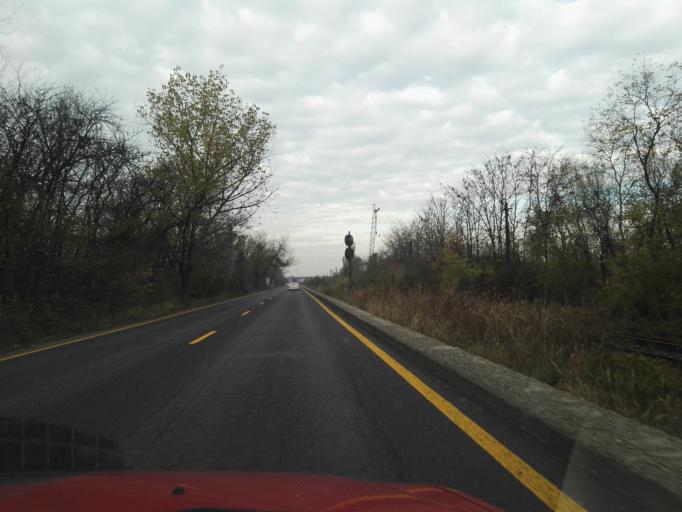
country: RO
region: Ilfov
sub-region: Comuna Magurele
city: Magurele
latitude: 44.3564
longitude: 26.0452
